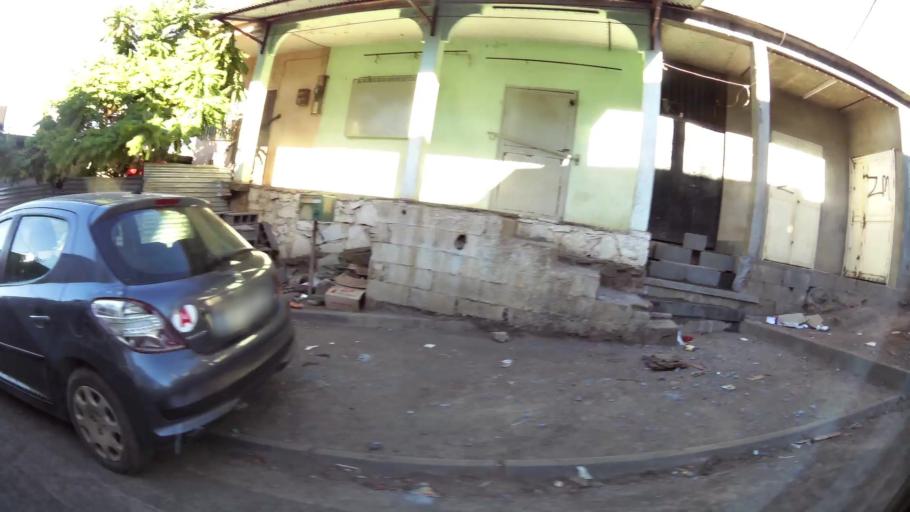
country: YT
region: Koungou
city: Koungou
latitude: -12.7464
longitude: 45.2204
